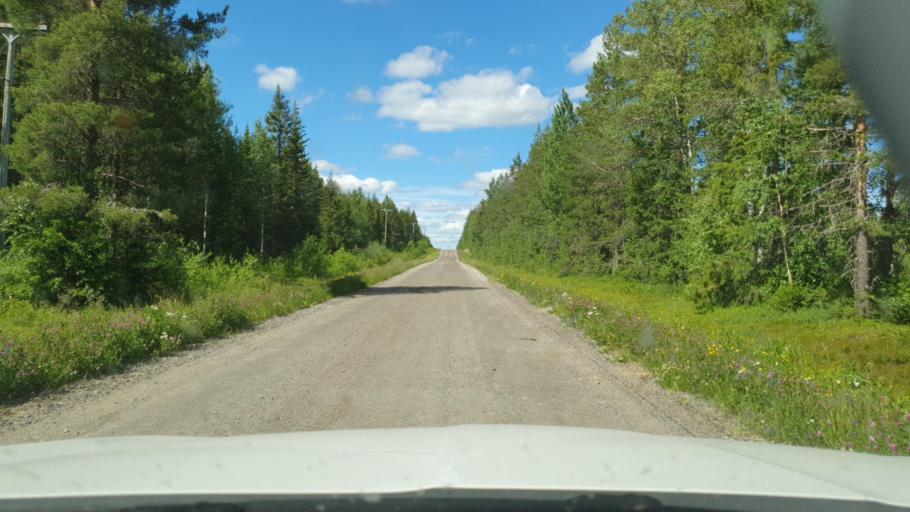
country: SE
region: Vaesterbotten
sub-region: Skelleftea Kommun
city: Backa
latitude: 65.1677
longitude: 21.1230
